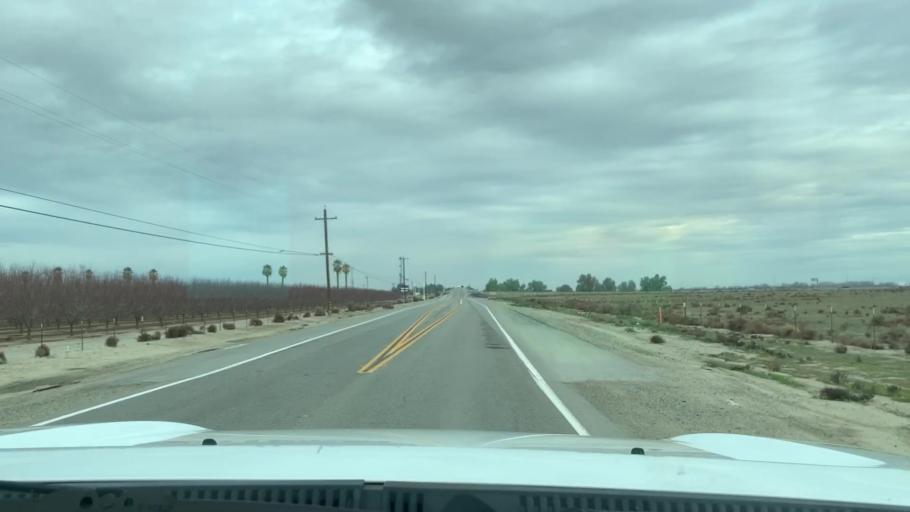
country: US
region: California
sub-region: Kern County
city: Rosedale
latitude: 35.2862
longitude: -119.2525
